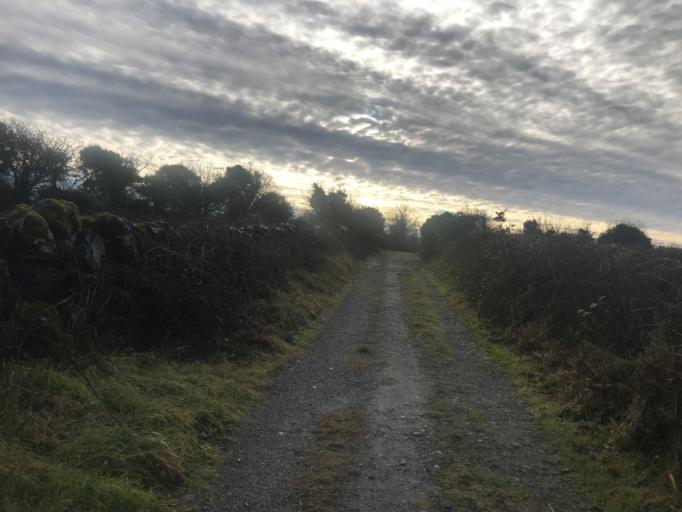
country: IE
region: Connaught
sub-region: County Galway
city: Claregalway
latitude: 53.3199
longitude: -9.0050
